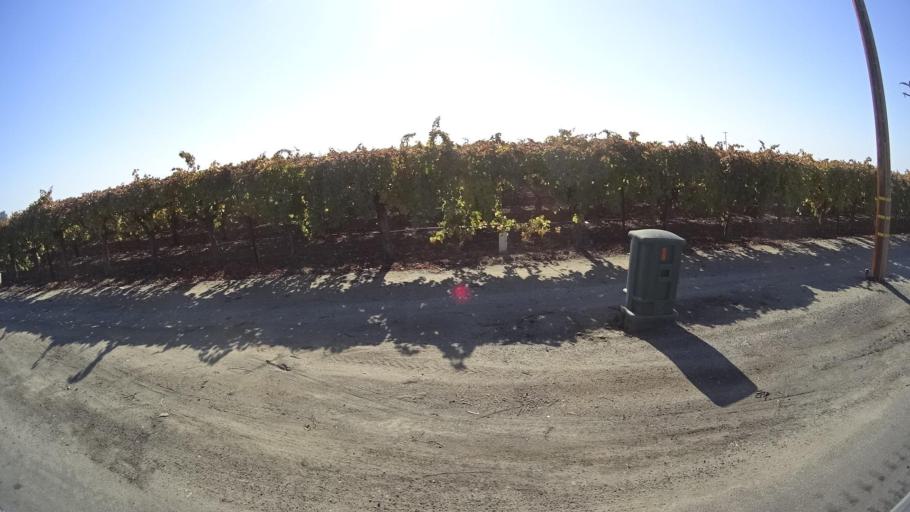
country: US
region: California
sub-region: Kern County
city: McFarland
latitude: 35.7180
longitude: -119.1593
